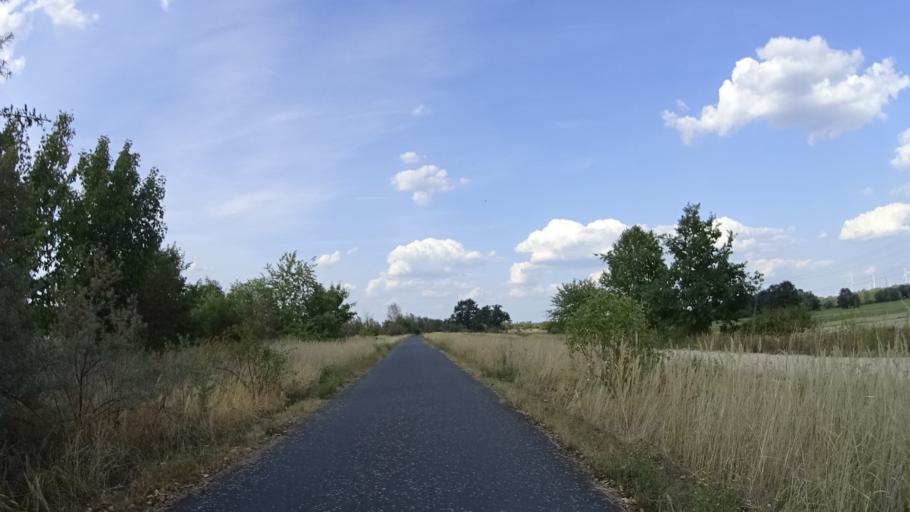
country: DE
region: Saxony
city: Ostritz
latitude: 51.0763
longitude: 14.9689
